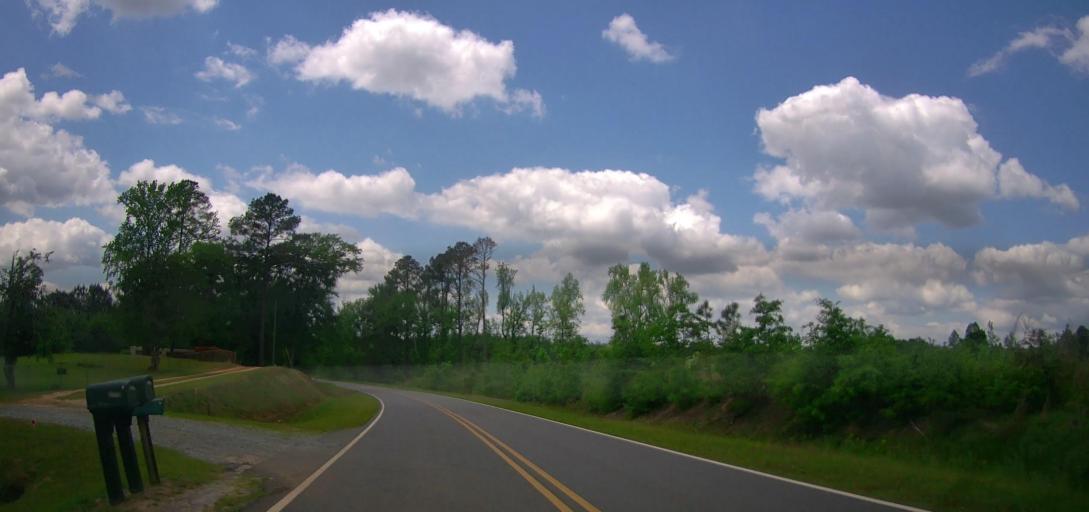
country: US
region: Georgia
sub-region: Laurens County
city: East Dublin
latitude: 32.6200
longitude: -82.8210
